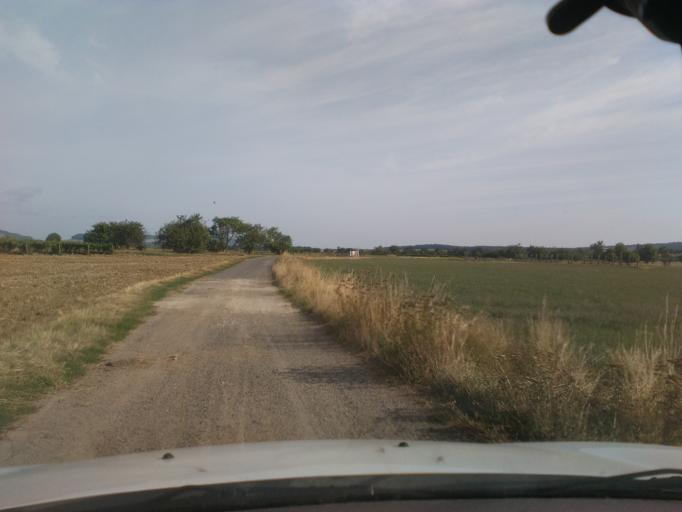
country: FR
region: Lorraine
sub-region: Departement des Vosges
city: Mirecourt
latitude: 48.3252
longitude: 6.0936
